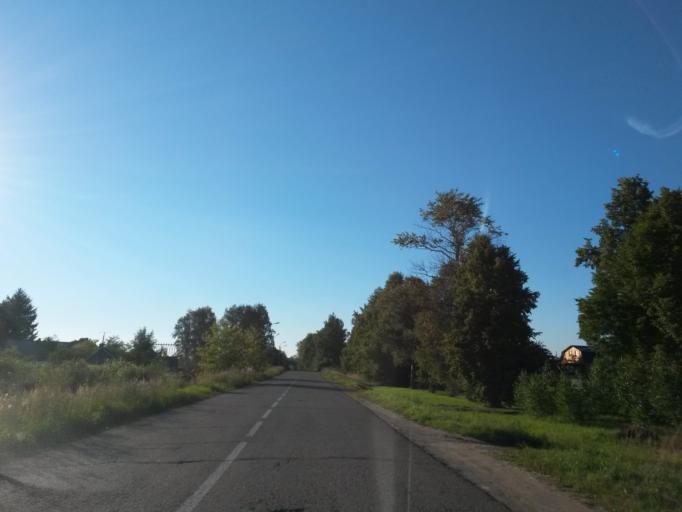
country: RU
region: Jaroslavl
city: Gavrilov-Yam
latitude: 57.2926
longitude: 39.8821
